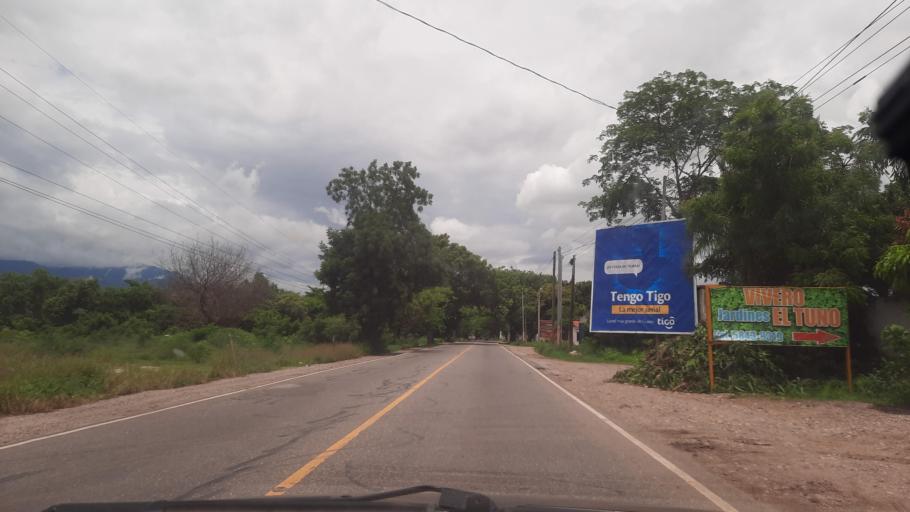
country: GT
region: Zacapa
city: Estanzuela
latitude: 14.9894
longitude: -89.5631
